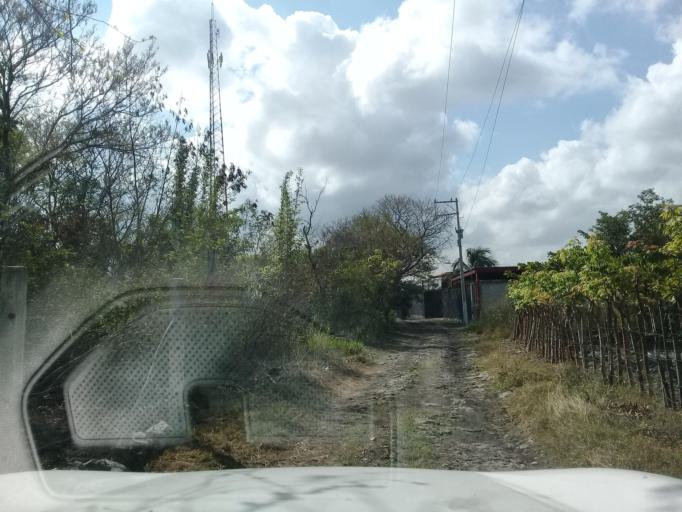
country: MX
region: Veracruz
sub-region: Emiliano Zapata
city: Plan del Rio
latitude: 19.4111
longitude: -96.6526
